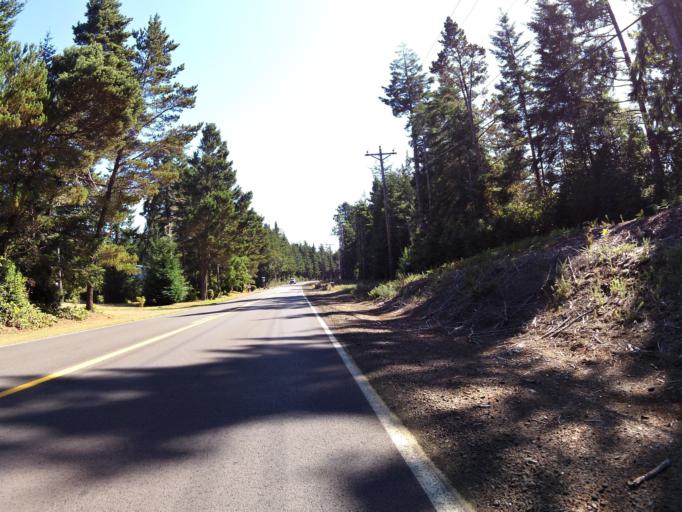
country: US
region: Oregon
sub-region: Coos County
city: Bandon
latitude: 43.2050
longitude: -124.3673
